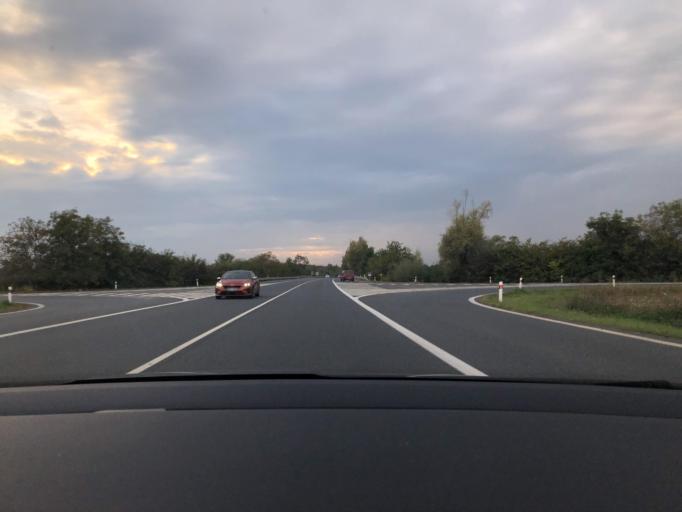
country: CZ
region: Central Bohemia
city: Planany
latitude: 50.0447
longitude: 15.0291
